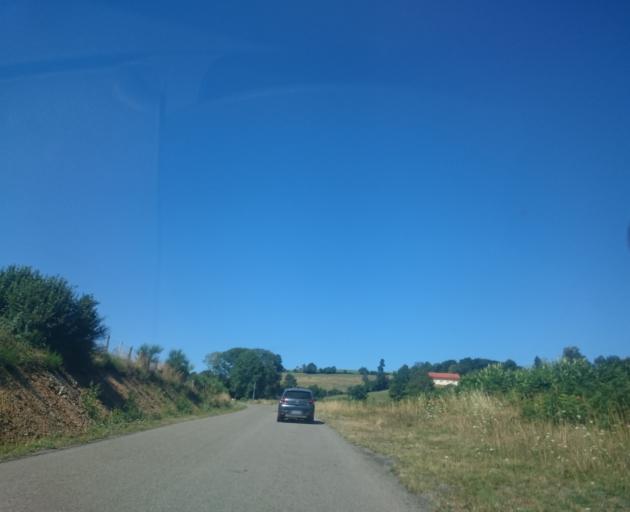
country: FR
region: Auvergne
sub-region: Departement du Cantal
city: Saint-Mamet-la-Salvetat
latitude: 44.8037
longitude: 2.3662
